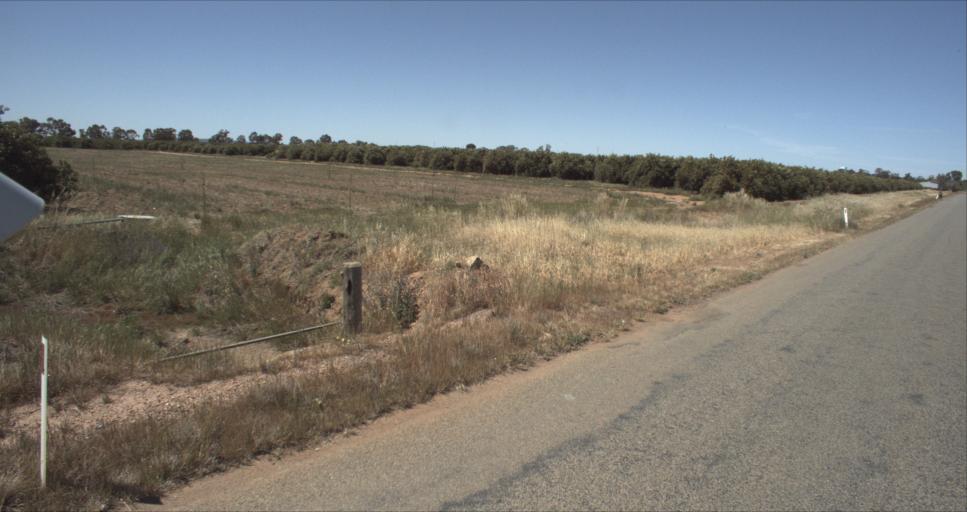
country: AU
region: New South Wales
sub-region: Leeton
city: Leeton
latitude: -34.5425
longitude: 146.3647
